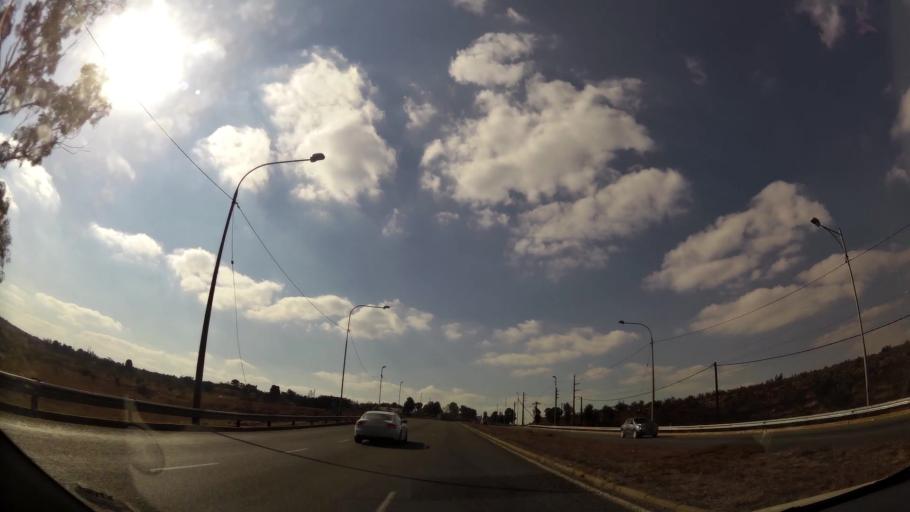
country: ZA
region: Gauteng
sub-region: West Rand District Municipality
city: Krugersdorp
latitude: -26.0657
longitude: 27.8050
